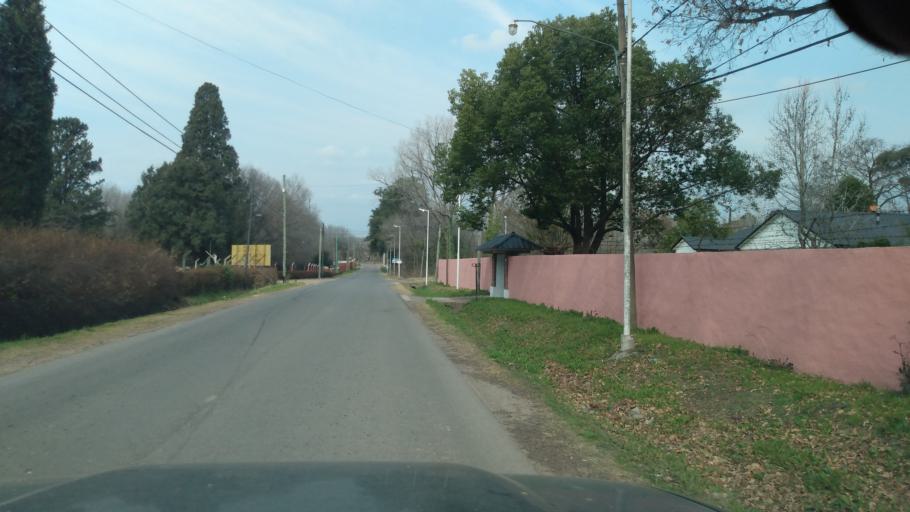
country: AR
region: Buenos Aires
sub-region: Partido de Lujan
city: Lujan
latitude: -34.5573
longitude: -59.1242
